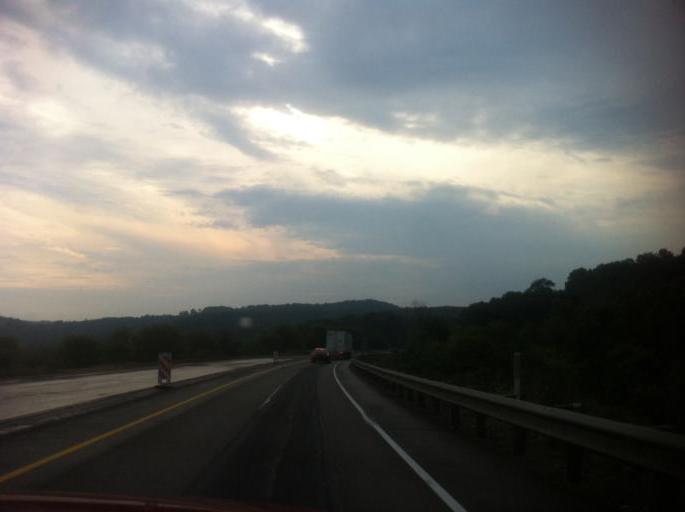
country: US
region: Pennsylvania
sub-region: Clarion County
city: Knox
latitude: 41.1848
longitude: -79.5514
